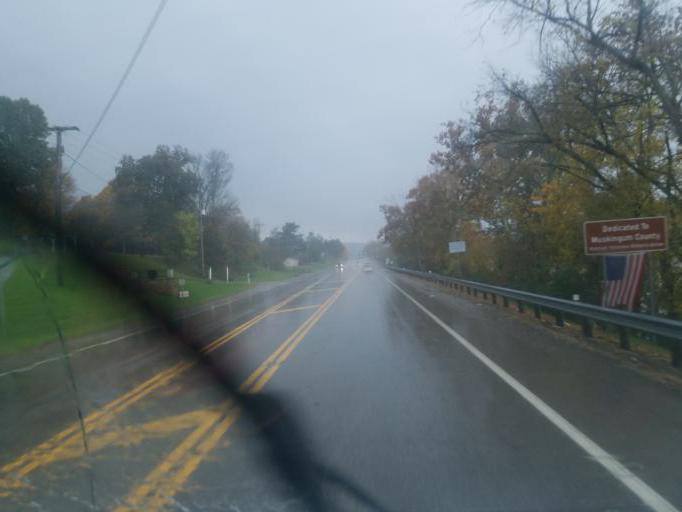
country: US
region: Ohio
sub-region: Muskingum County
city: South Zanesville
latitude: 39.9163
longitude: -82.0016
